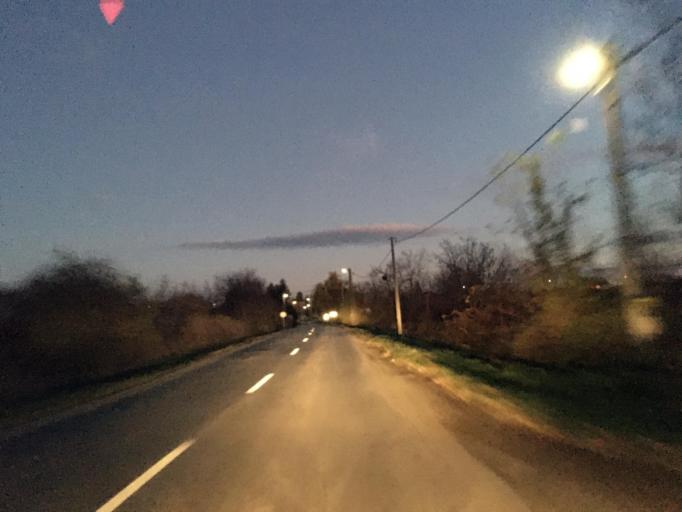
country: SK
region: Nitriansky
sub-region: Okres Komarno
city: Hurbanovo
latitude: 47.8909
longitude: 18.1962
